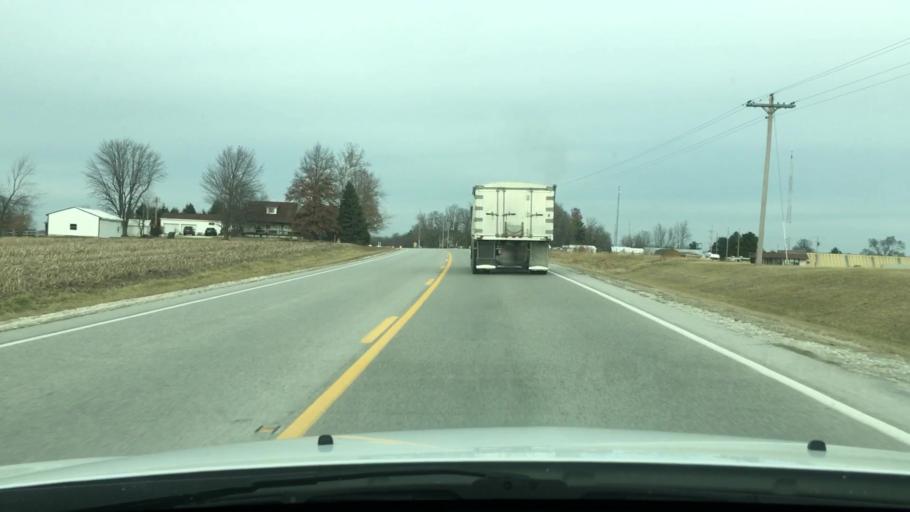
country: US
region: Illinois
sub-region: Pike County
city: Pittsfield
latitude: 39.6458
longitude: -90.7845
